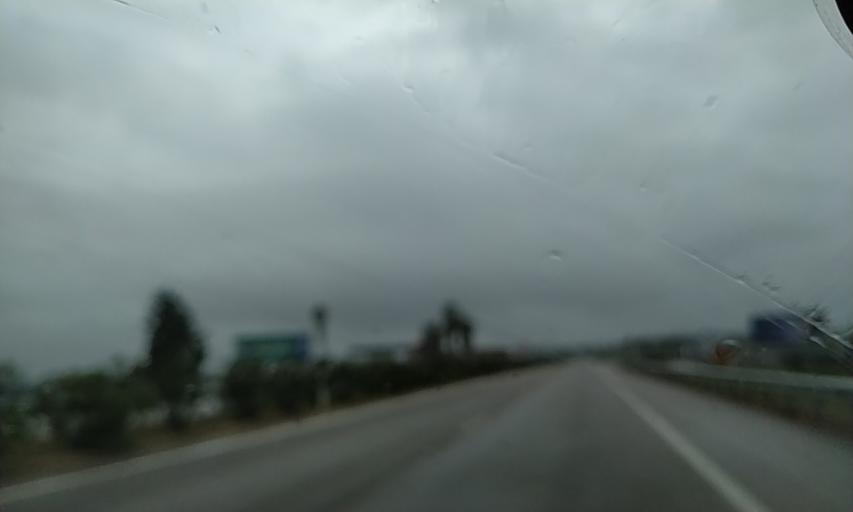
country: ES
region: Extremadura
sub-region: Provincia de Badajoz
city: Badajoz
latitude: 38.9079
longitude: -6.9649
